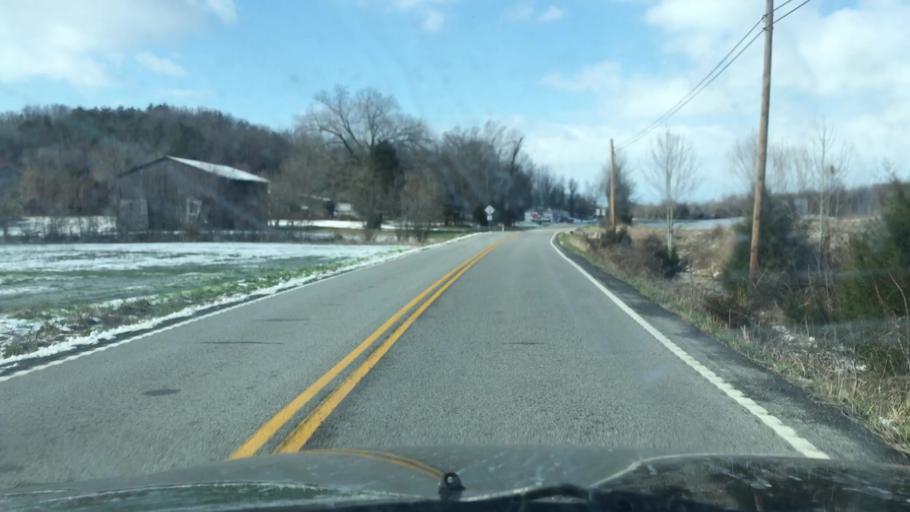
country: US
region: Kentucky
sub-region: Marion County
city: Lebanon
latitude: 37.5231
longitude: -85.3028
